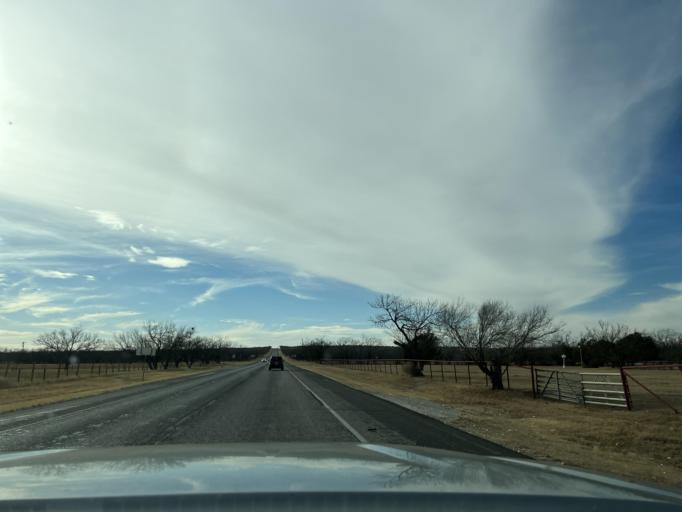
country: US
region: Texas
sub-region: Fisher County
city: Roby
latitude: 32.7601
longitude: -100.3138
